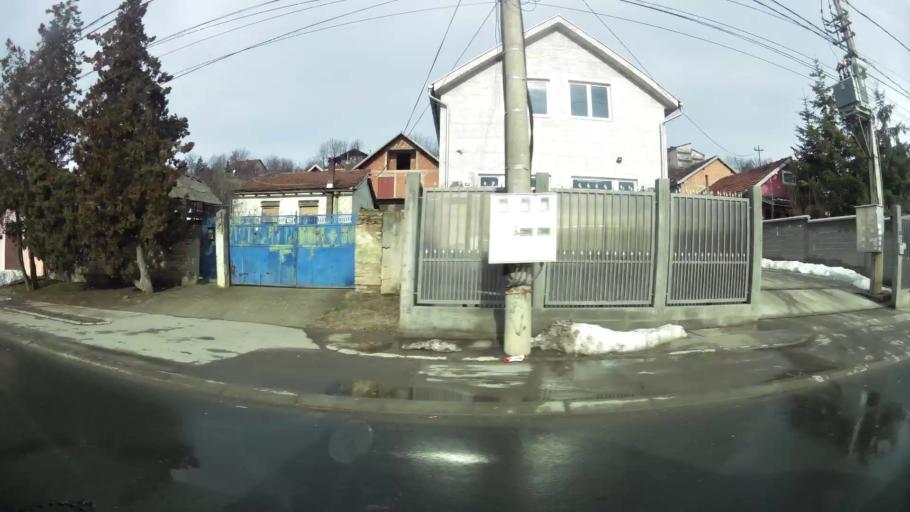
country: RS
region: Central Serbia
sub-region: Belgrade
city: Zemun
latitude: 44.7998
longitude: 20.3556
